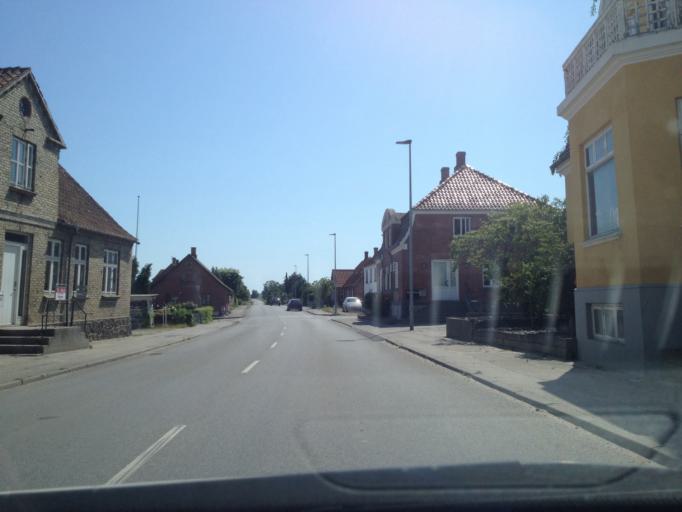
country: DK
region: Central Jutland
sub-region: Samso Kommune
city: Tranebjerg
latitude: 55.8501
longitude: 10.5711
